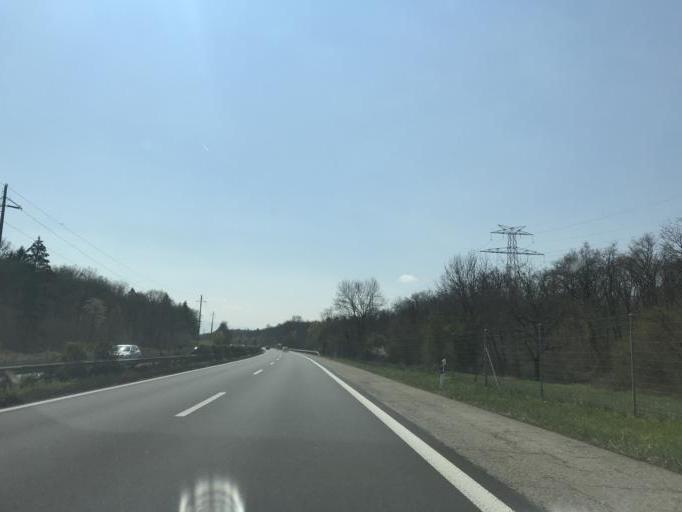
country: FR
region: Rhone-Alpes
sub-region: Departement de l'Ain
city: Sauverny
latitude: 46.3139
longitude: 6.1444
